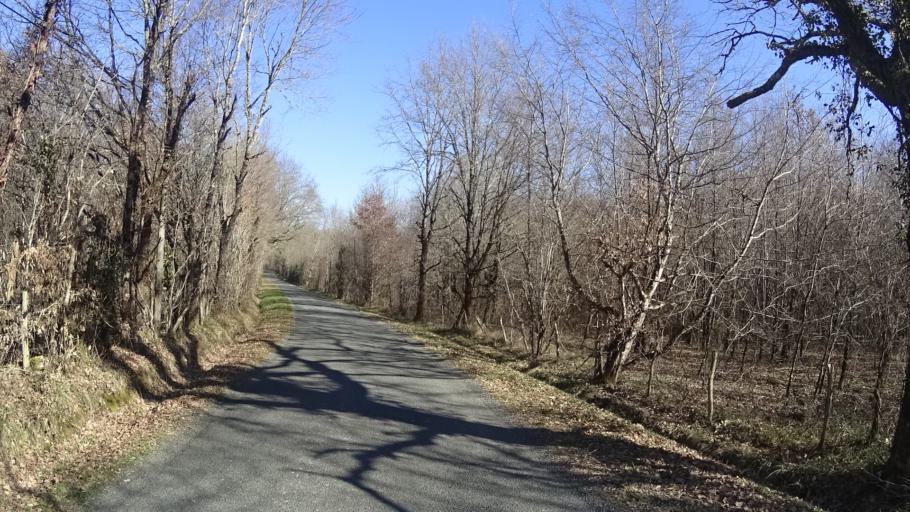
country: FR
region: Aquitaine
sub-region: Departement de la Dordogne
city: Montpon-Menesterol
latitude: 45.1055
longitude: 0.2082
